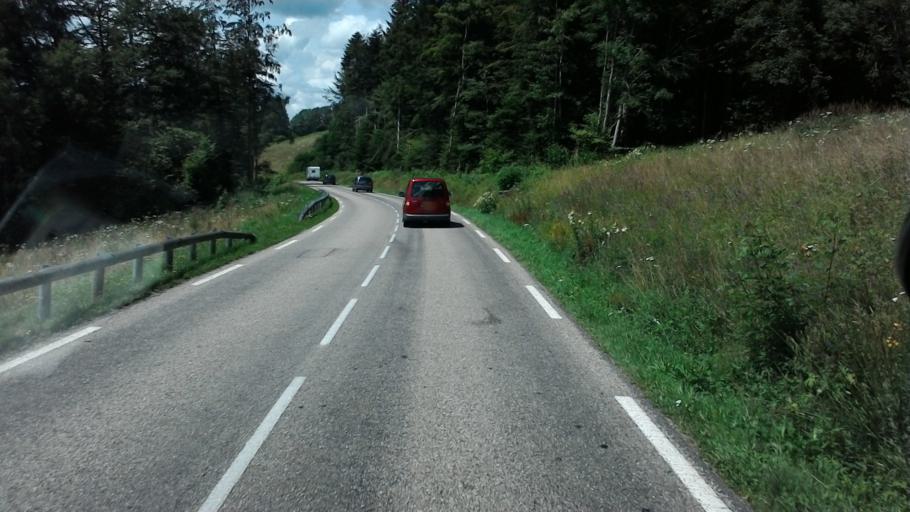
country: FR
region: Lorraine
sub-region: Departement des Vosges
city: Le Tholy
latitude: 48.0984
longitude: 6.7131
